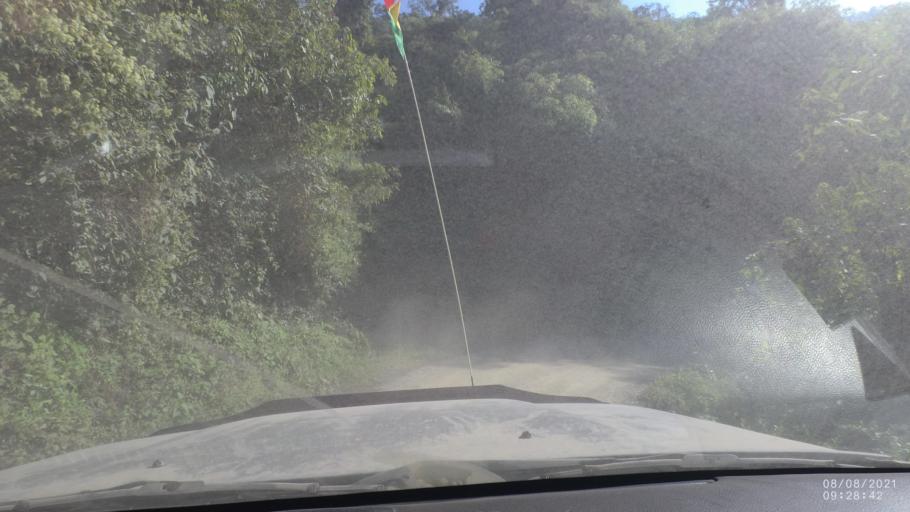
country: BO
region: La Paz
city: Quime
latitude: -16.5867
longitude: -66.7140
